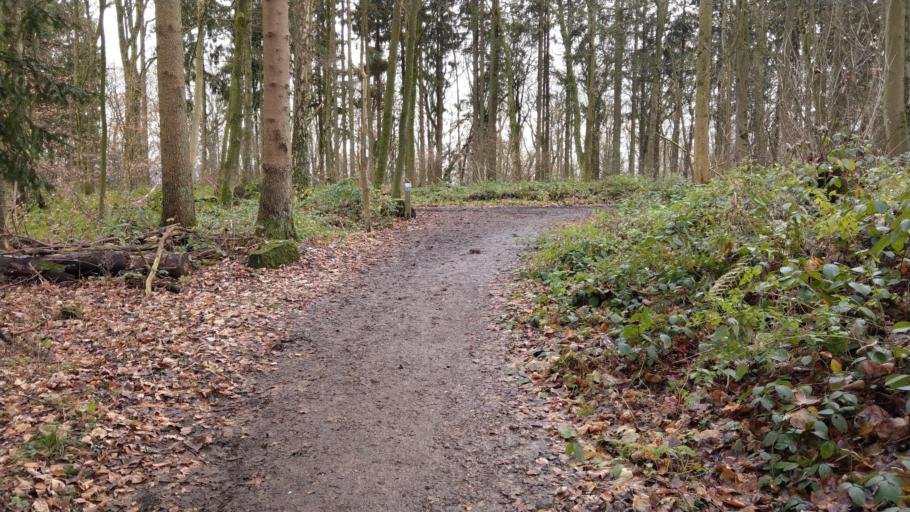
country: DE
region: North Rhine-Westphalia
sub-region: Regierungsbezirk Koln
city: Aachen
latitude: 50.7337
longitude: 6.0725
